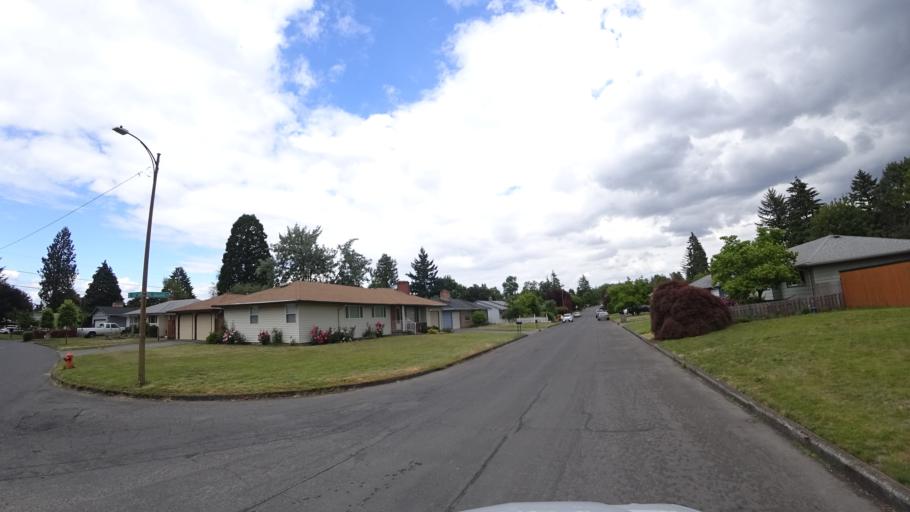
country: US
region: Oregon
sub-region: Clackamas County
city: Happy Valley
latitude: 45.5017
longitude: -122.4987
